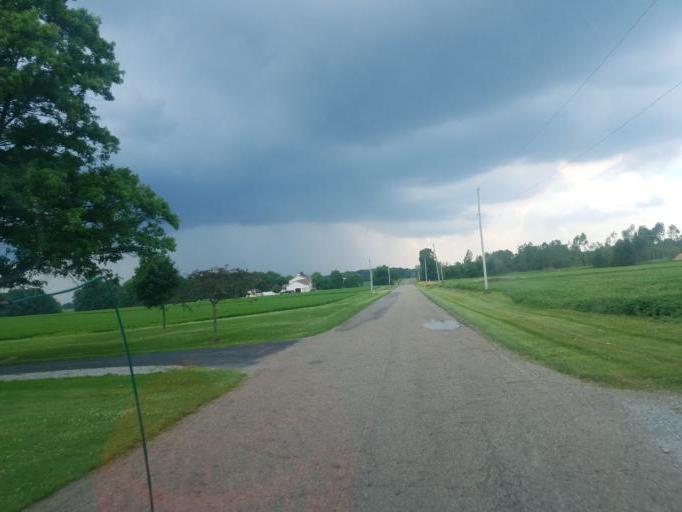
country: US
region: Ohio
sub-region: Mahoning County
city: Sebring
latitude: 40.9741
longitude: -80.9610
